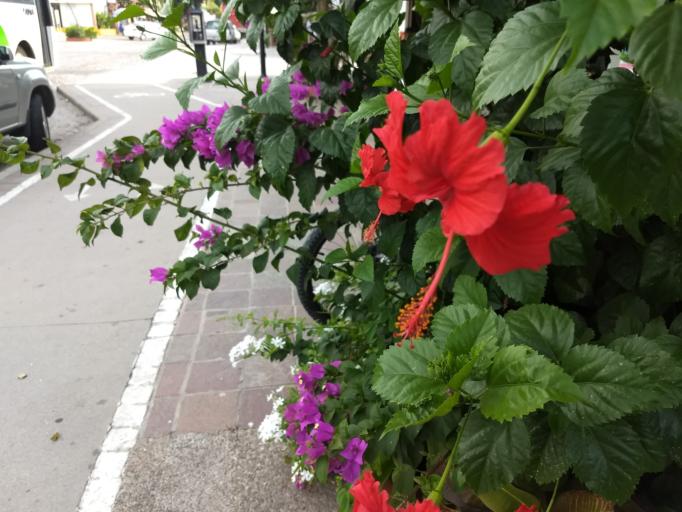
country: MX
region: Jalisco
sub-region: Puerto Vallarta
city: Puerto Vallarta
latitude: 20.6192
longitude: -105.2312
